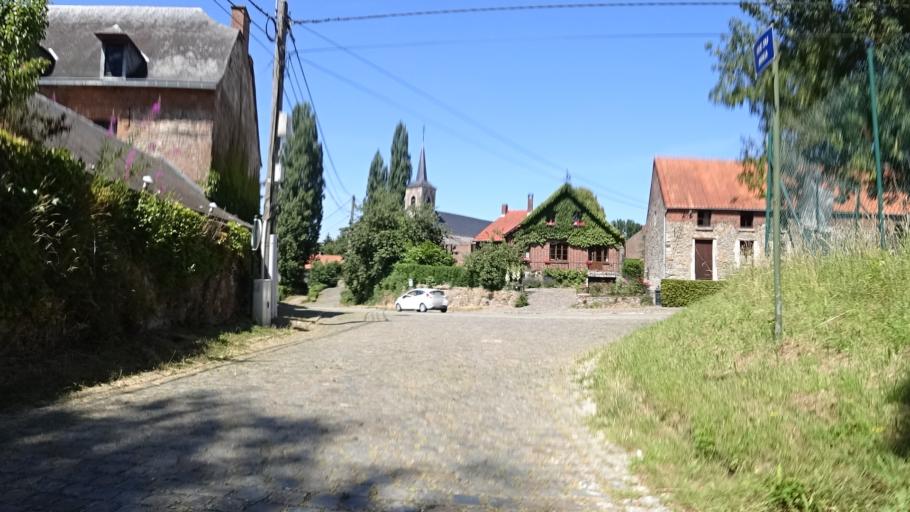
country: BE
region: Wallonia
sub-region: Province du Brabant Wallon
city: Jodoigne
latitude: 50.6861
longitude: 4.8436
